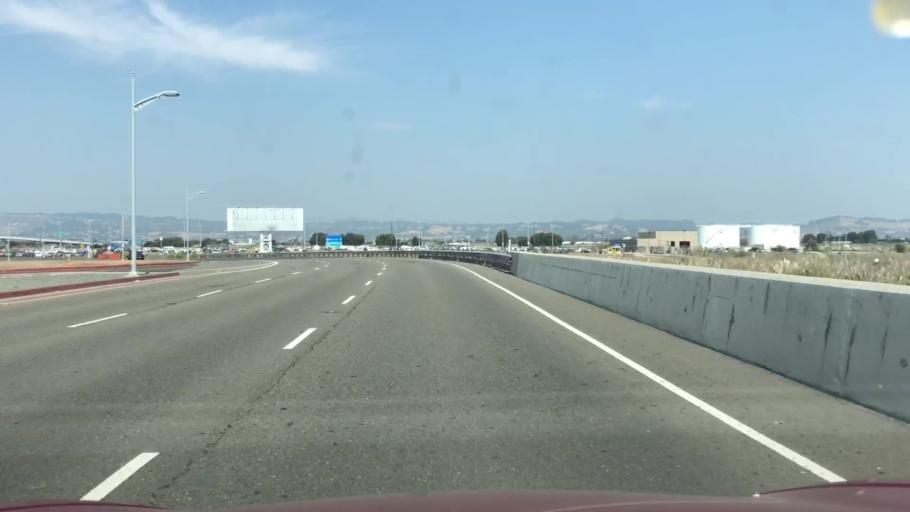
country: US
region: California
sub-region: Alameda County
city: San Leandro
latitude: 37.7124
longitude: -122.2086
